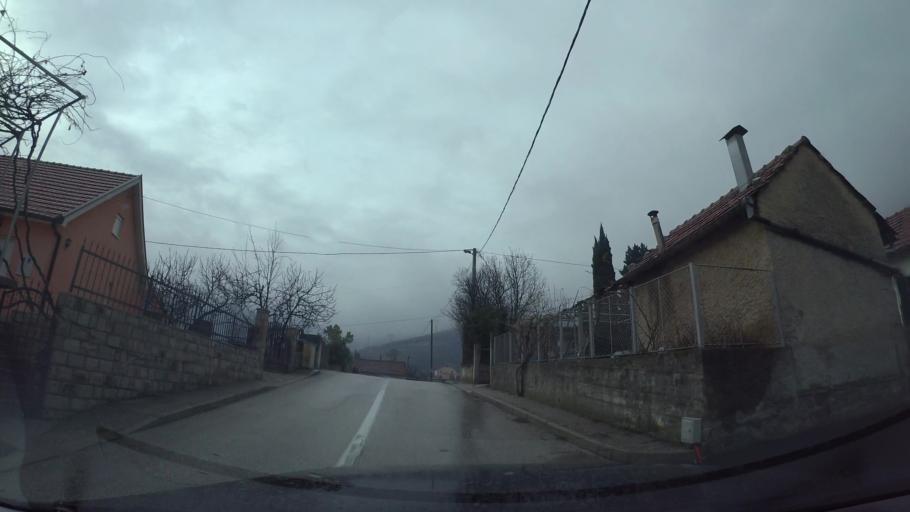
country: BA
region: Federation of Bosnia and Herzegovina
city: Cim
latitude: 43.3551
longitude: 17.7749
